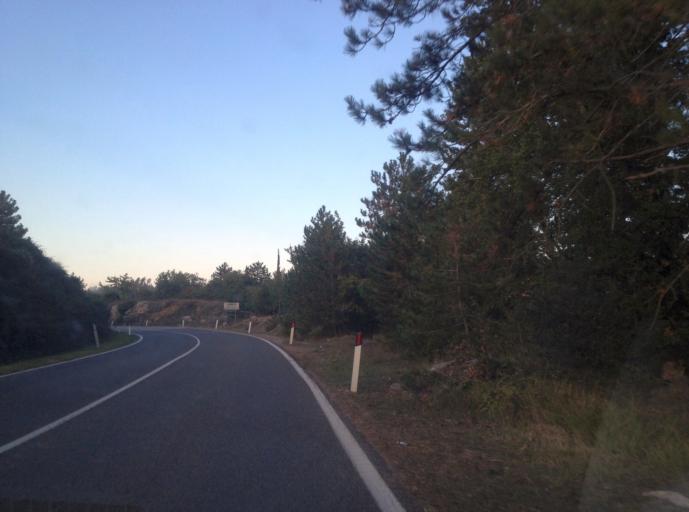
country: IT
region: Tuscany
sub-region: Provincia di Siena
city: Castellina in Chianti
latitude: 43.4530
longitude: 11.2923
